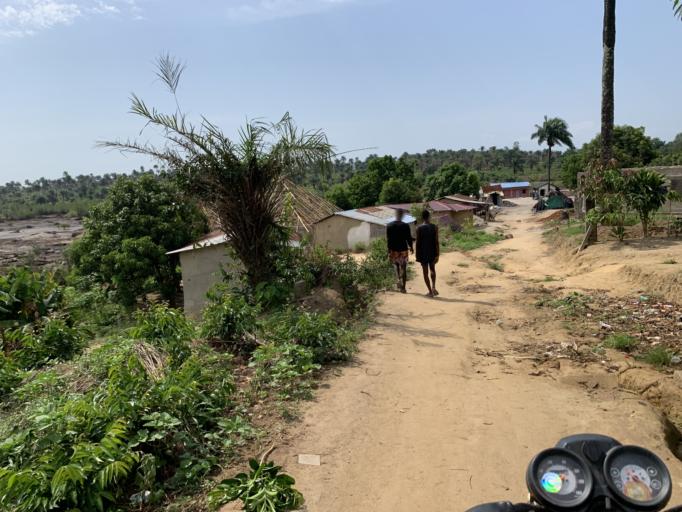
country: SL
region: Western Area
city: Waterloo
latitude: 8.3496
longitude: -13.0529
